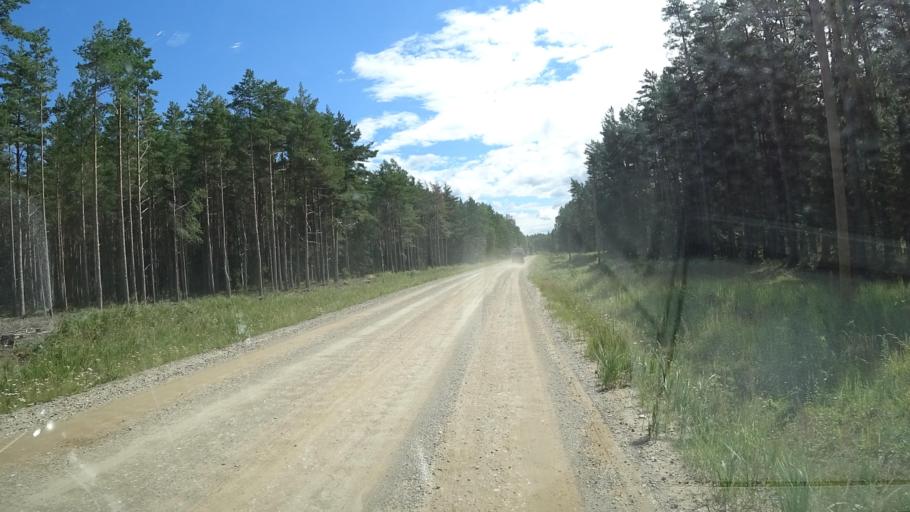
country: LV
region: Ventspils
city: Ventspils
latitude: 57.4886
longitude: 21.6674
